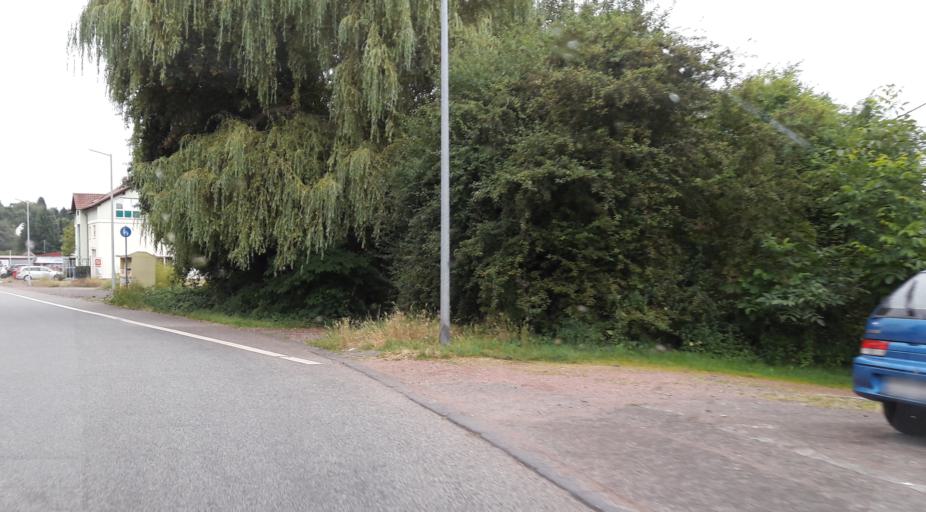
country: DE
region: Saarland
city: Neunkirchen
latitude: 49.3676
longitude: 7.1837
